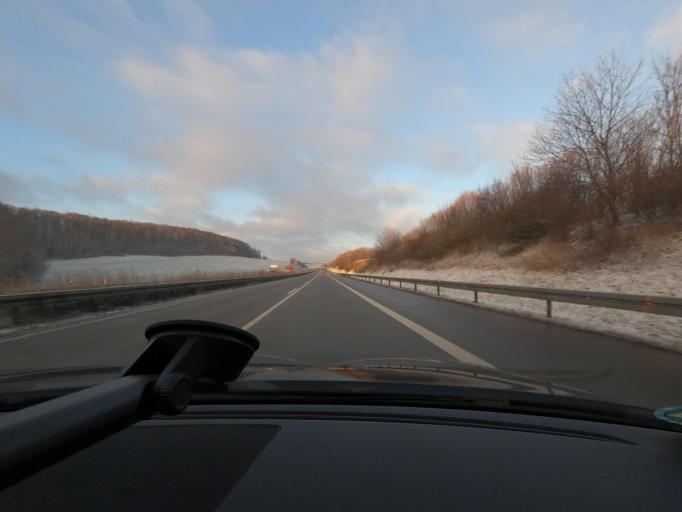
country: DE
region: Thuringia
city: Steinheuterode
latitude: 51.3945
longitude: 10.0935
